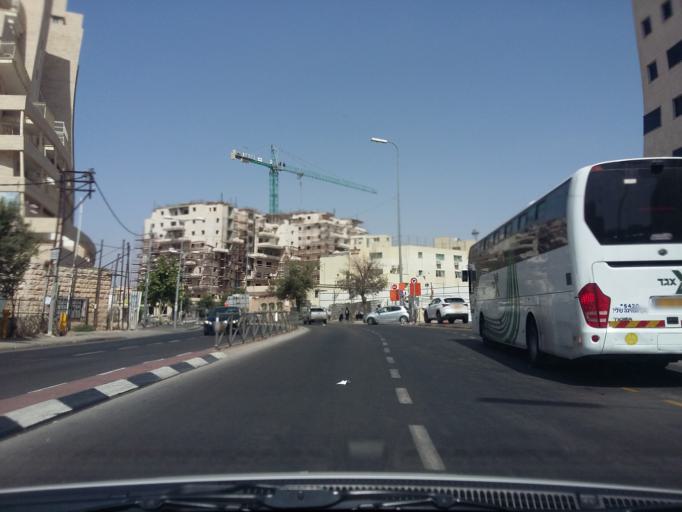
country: IL
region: Jerusalem
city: West Jerusalem
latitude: 31.7910
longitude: 35.2021
